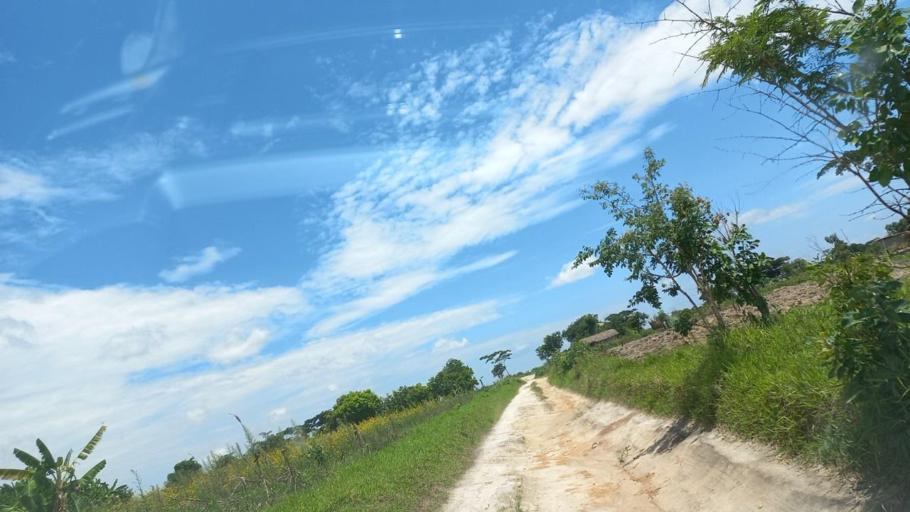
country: ZM
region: Copperbelt
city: Ndola
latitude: -12.8687
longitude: 28.4353
